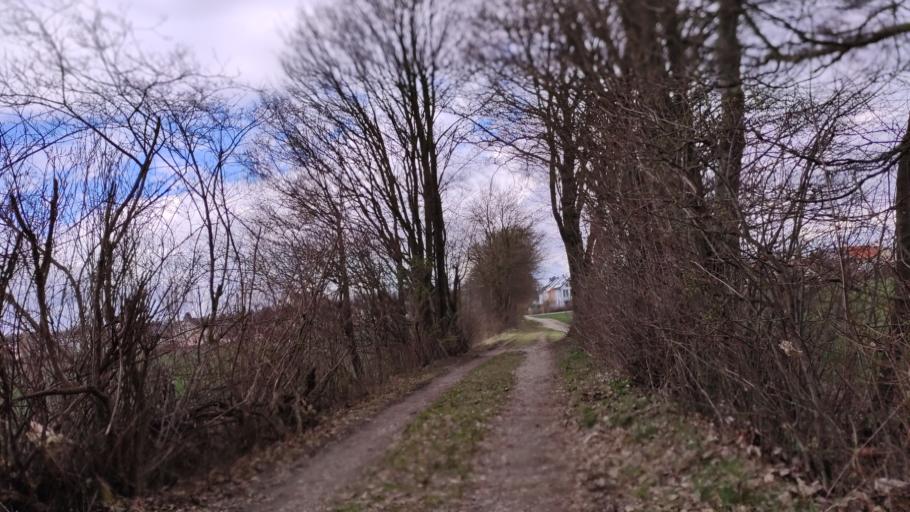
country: DE
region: Bavaria
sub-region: Upper Bavaria
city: Emmering
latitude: 48.1751
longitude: 11.2803
